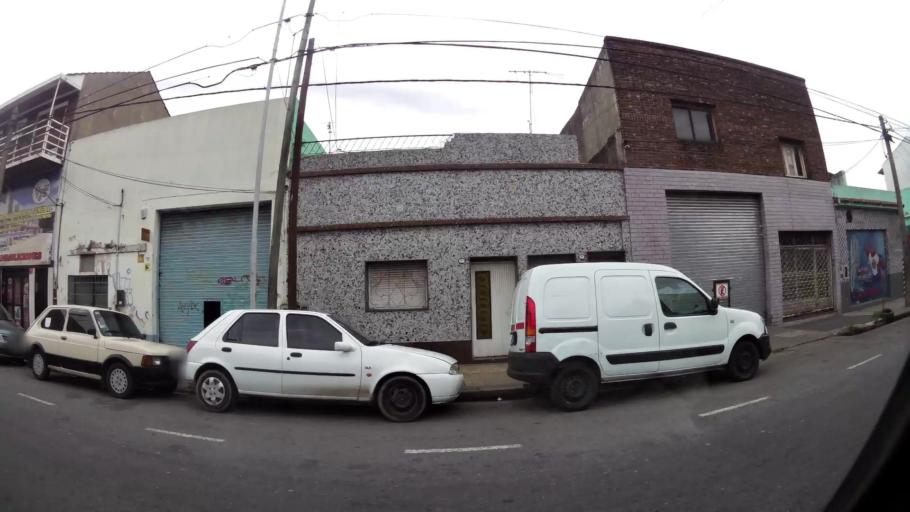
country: AR
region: Buenos Aires
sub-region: Partido de Avellaneda
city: Avellaneda
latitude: -34.6727
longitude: -58.3931
